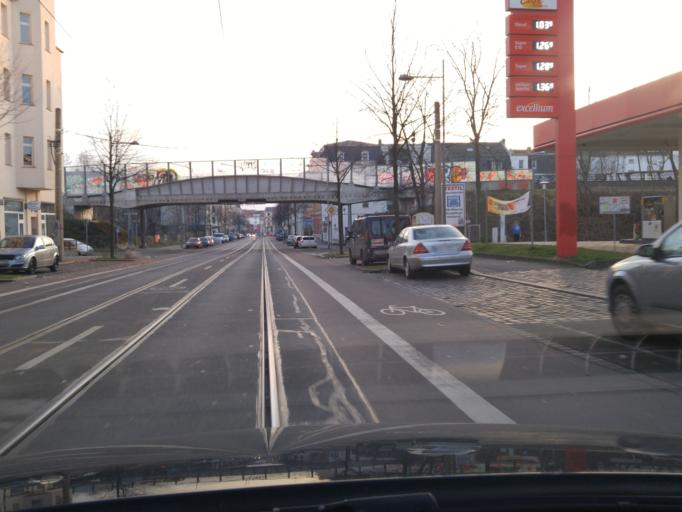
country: DE
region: Saxony
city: Leipzig
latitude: 51.3663
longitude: 12.3665
